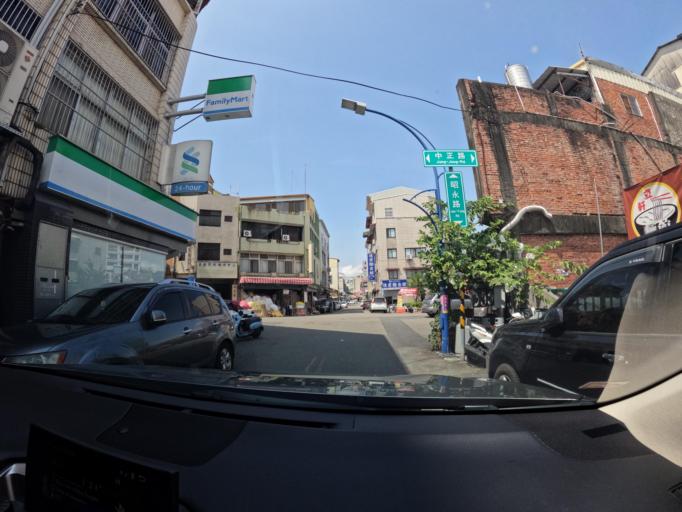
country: TW
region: Taiwan
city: Fengyuan
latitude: 24.3111
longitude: 120.8261
